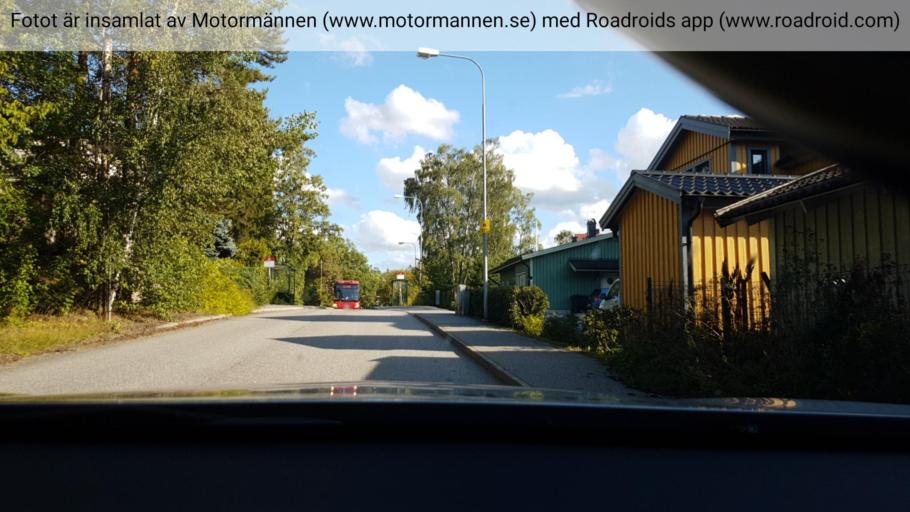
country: SE
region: Stockholm
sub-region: Huddinge Kommun
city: Huddinge
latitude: 59.2308
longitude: 17.9773
